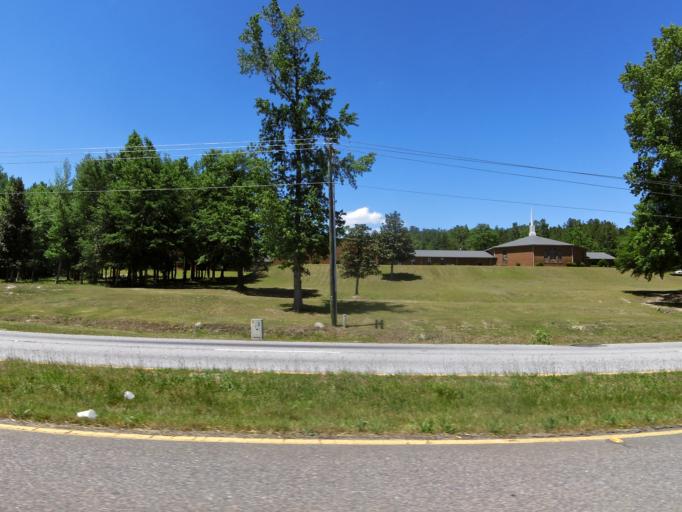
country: US
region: South Carolina
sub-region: Aiken County
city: Clearwater
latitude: 33.5098
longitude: -81.8728
